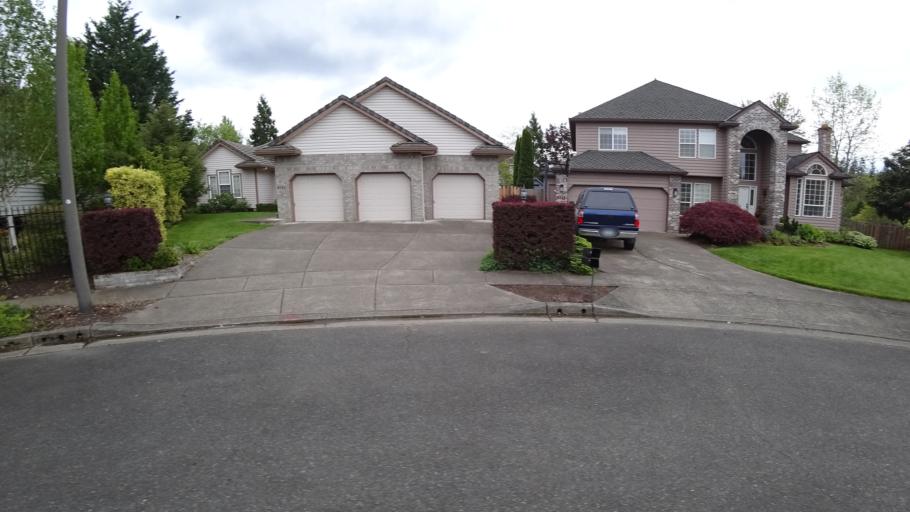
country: US
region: Oregon
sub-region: Washington County
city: Beaverton
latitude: 45.4571
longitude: -122.8331
